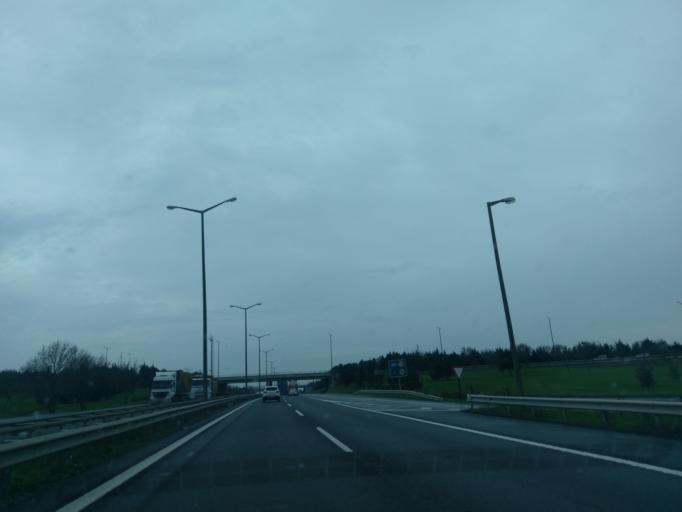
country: TR
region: Istanbul
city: Silivri
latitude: 41.1104
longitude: 28.2666
